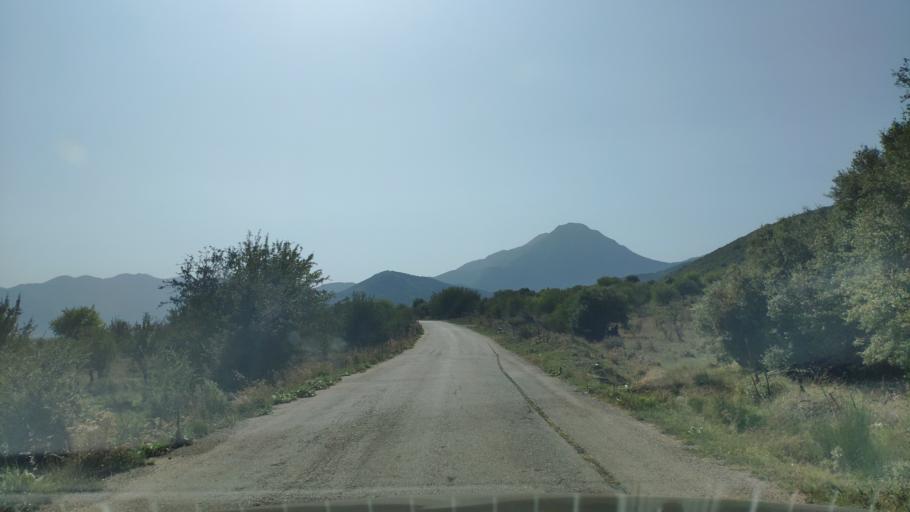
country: GR
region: West Greece
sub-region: Nomos Achaias
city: Aiyira
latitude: 37.9570
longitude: 22.3416
